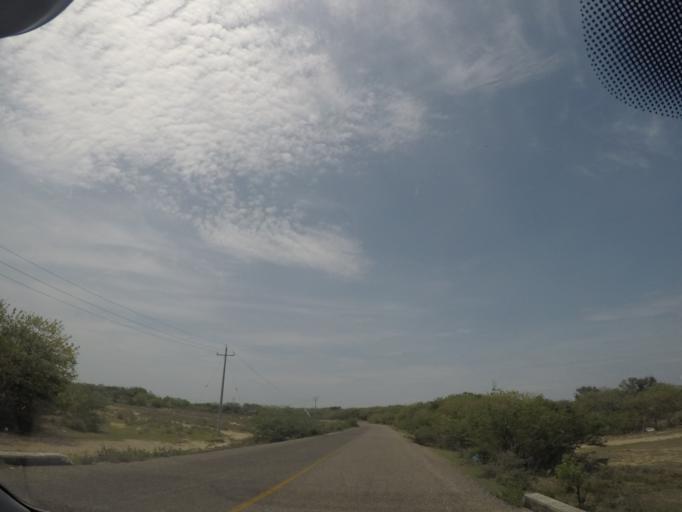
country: MX
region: Oaxaca
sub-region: San Mateo del Mar
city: Colonia Juarez
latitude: 16.2108
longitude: -95.0470
